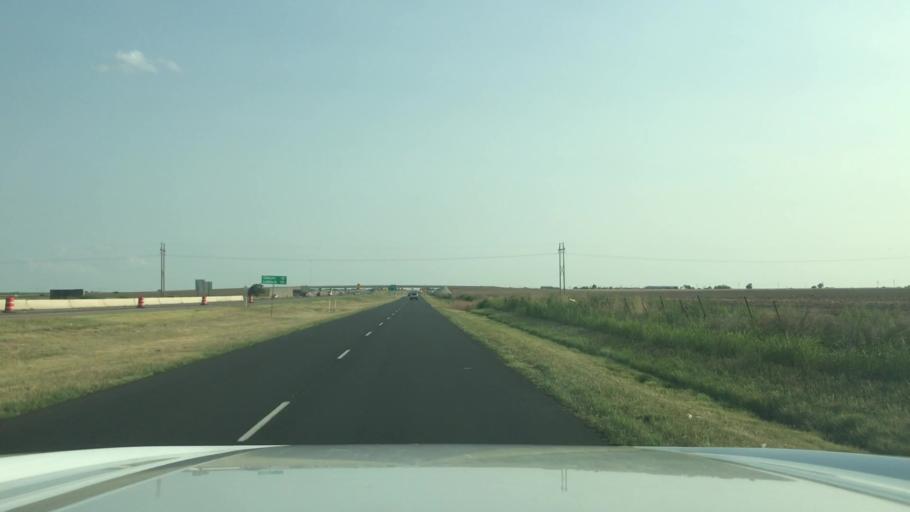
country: US
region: Texas
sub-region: Randall County
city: Canyon
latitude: 35.1088
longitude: -101.9119
